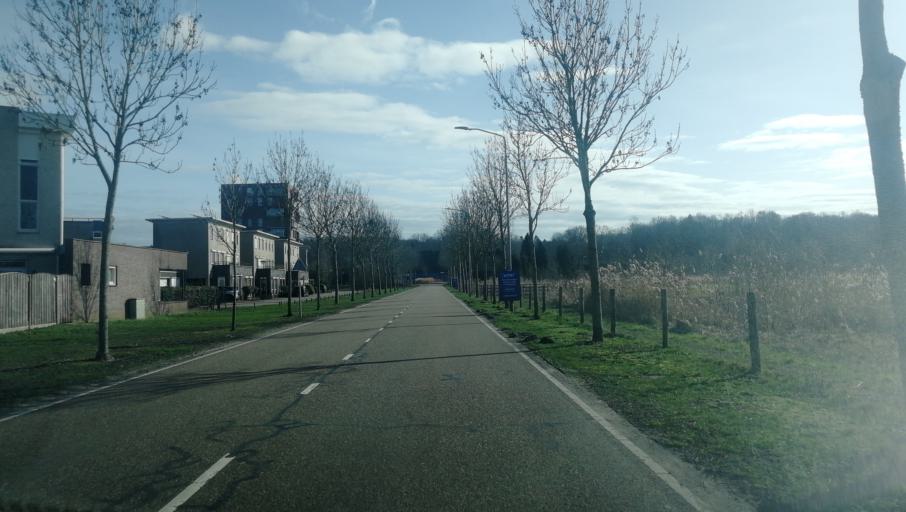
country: NL
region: Limburg
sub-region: Gemeente Venlo
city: Venlo
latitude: 51.3533
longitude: 6.1675
